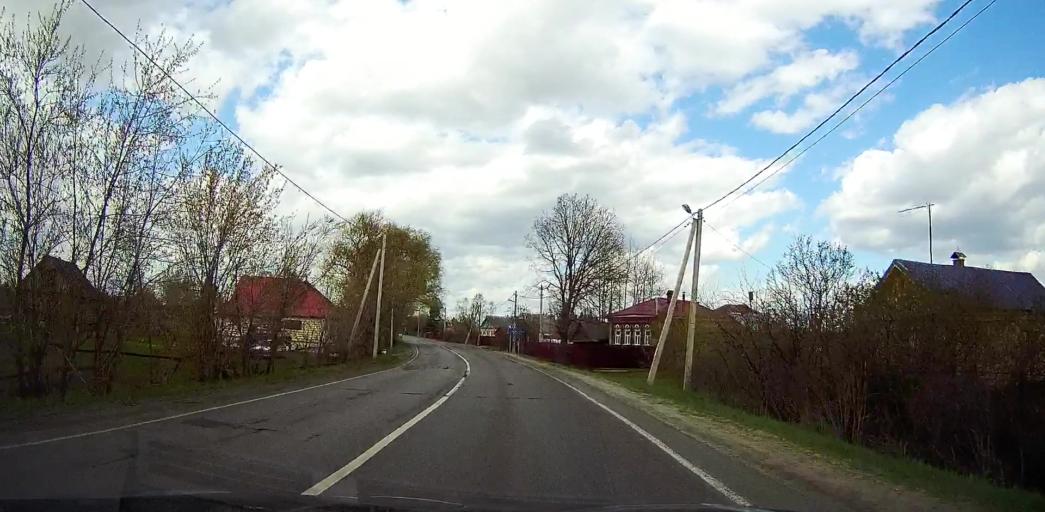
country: RU
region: Moskovskaya
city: Davydovo
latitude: 55.6341
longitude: 38.8692
